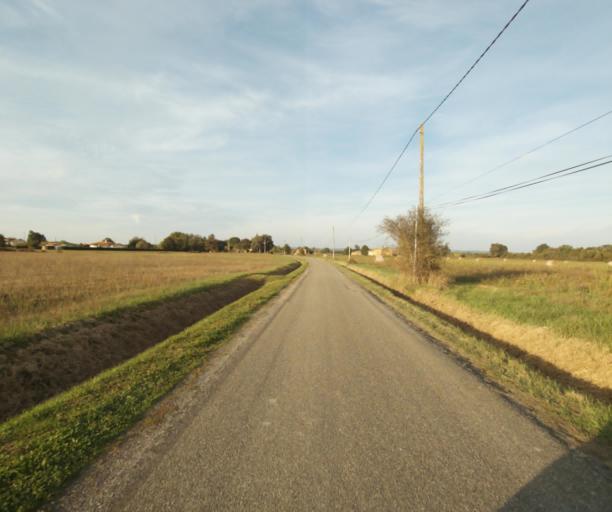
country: FR
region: Midi-Pyrenees
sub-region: Departement du Tarn-et-Garonne
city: Campsas
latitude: 43.8805
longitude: 1.3512
